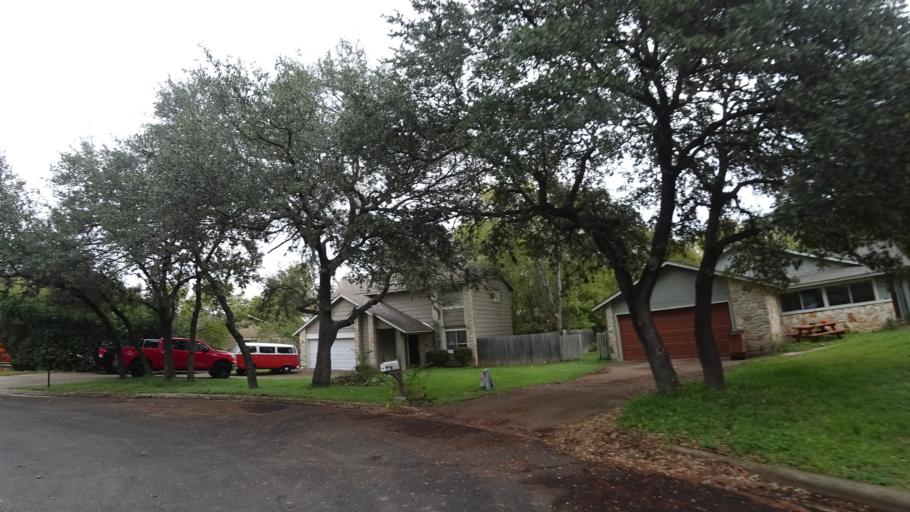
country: US
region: Texas
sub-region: Travis County
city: Shady Hollow
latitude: 30.2089
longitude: -97.8392
